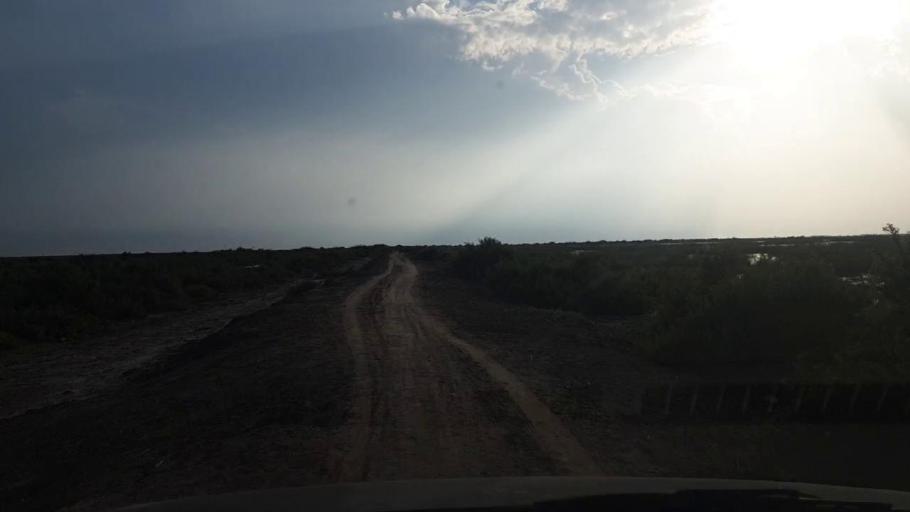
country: PK
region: Sindh
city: Badin
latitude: 24.4319
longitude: 68.6696
